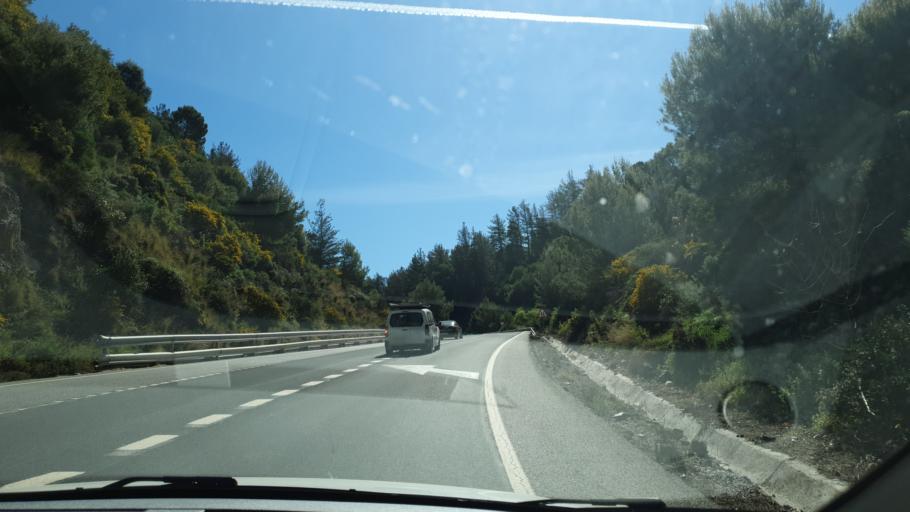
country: ES
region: Andalusia
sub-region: Provincia de Malaga
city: Ojen
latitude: 36.5749
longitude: -4.8609
